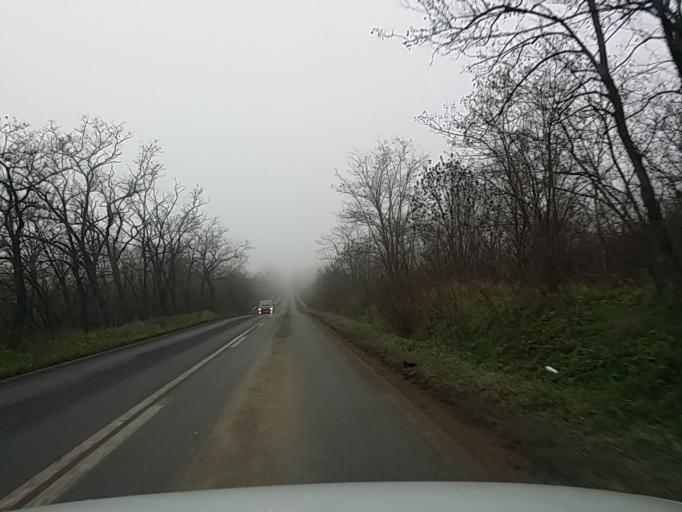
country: HU
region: Pest
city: Budakeszi
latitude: 47.5190
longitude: 18.9123
